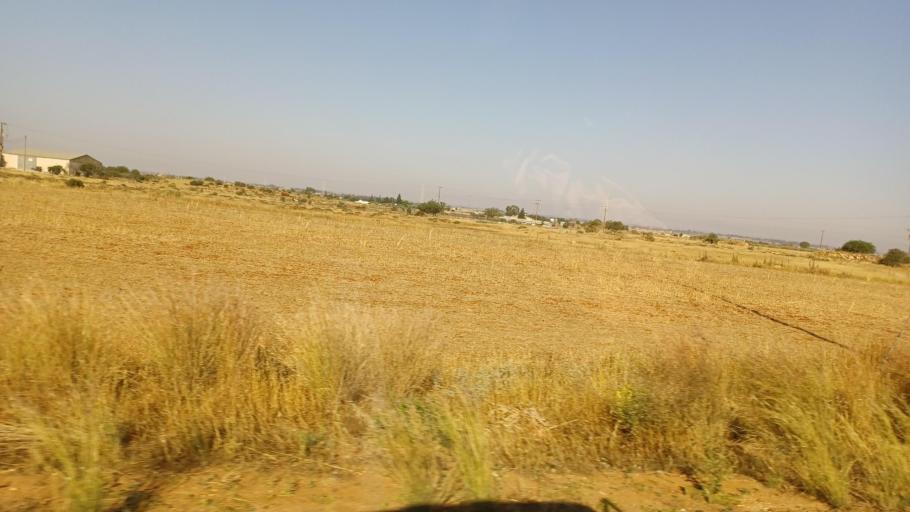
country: CY
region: Ammochostos
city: Frenaros
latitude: 35.0622
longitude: 33.9035
